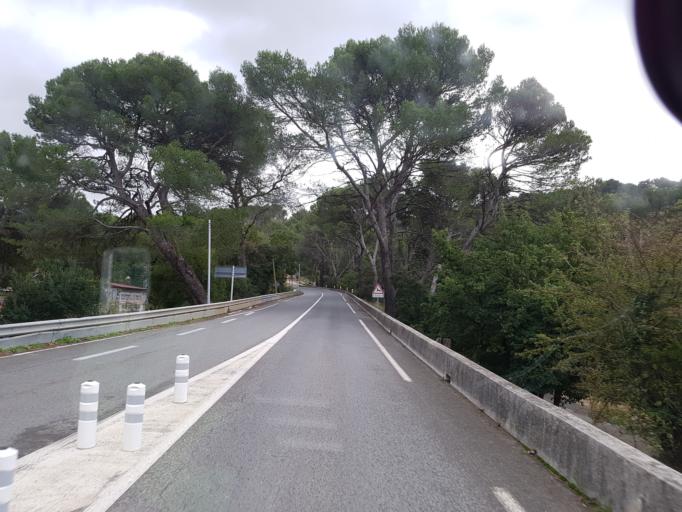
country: FR
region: Provence-Alpes-Cote d'Azur
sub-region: Departement des Bouches-du-Rhone
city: Cuges-les-Pins
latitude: 43.2672
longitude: 5.7278
